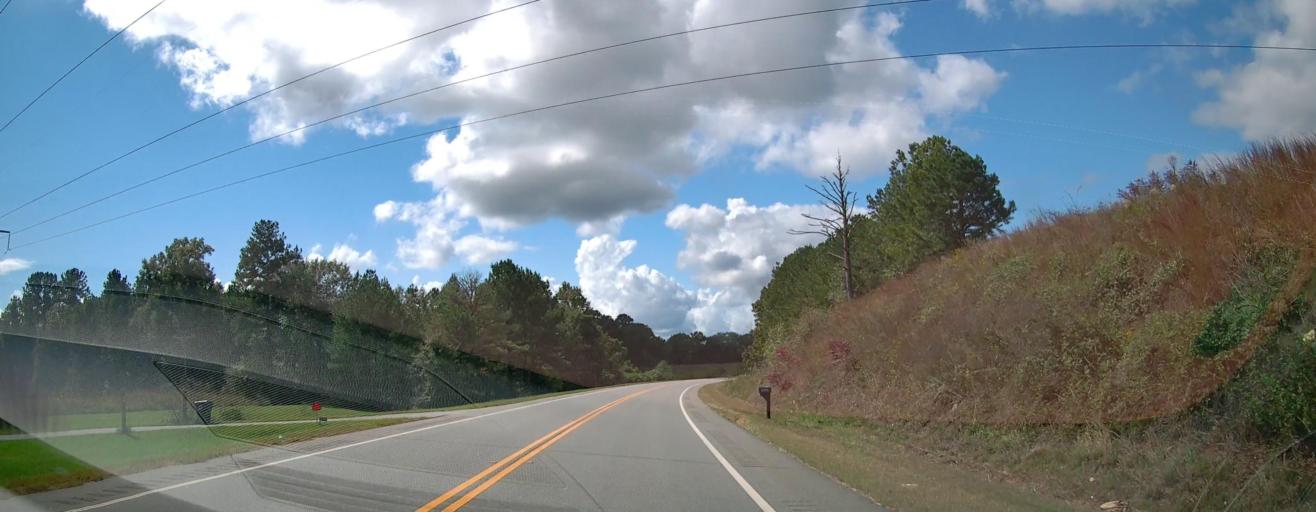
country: US
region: Georgia
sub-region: Baldwin County
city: Milledgeville
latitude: 33.0733
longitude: -83.3200
